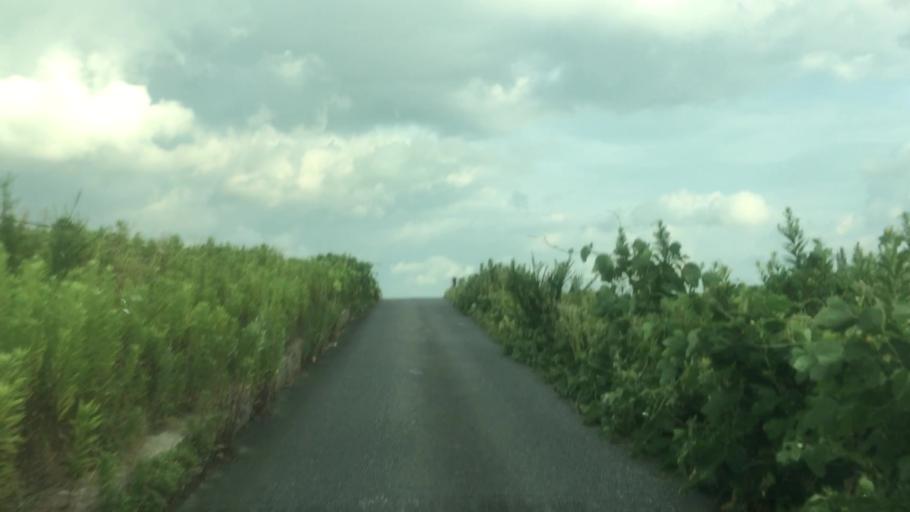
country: JP
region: Hyogo
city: Toyooka
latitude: 35.5643
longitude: 134.8119
